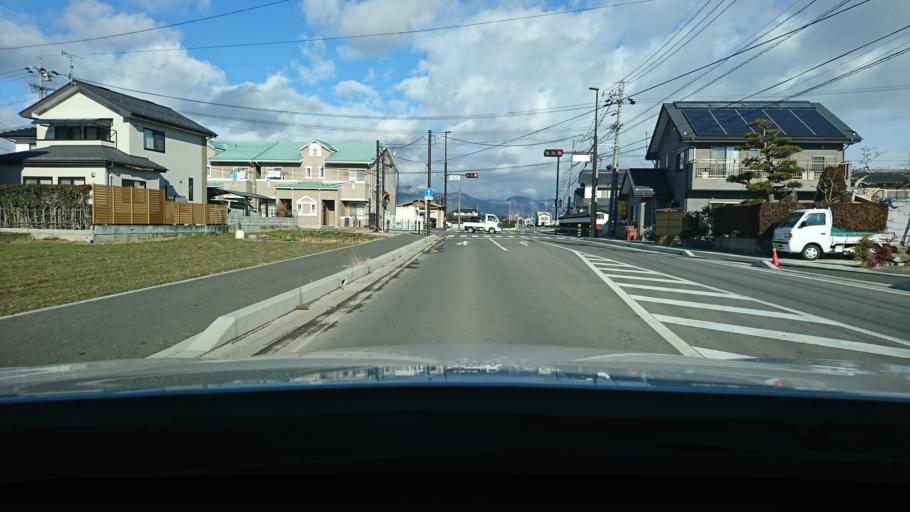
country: JP
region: Nagano
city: Nagano-shi
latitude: 36.5774
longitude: 138.1762
